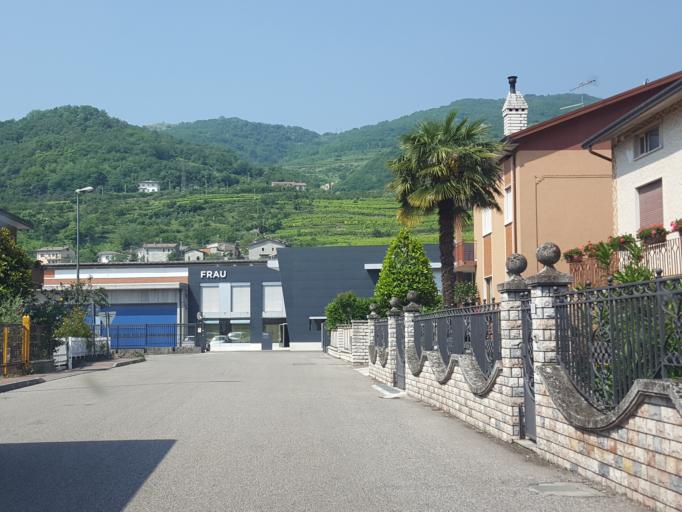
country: IT
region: Veneto
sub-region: Provincia di Verona
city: San Giovanni Ilarione
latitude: 45.5194
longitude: 11.2366
